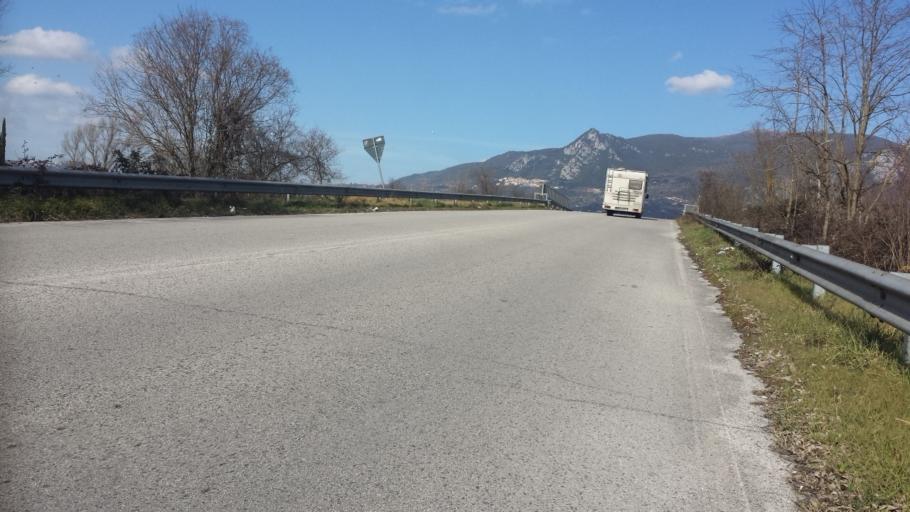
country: IT
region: Umbria
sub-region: Provincia di Terni
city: Terni
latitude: 42.5681
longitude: 12.5976
